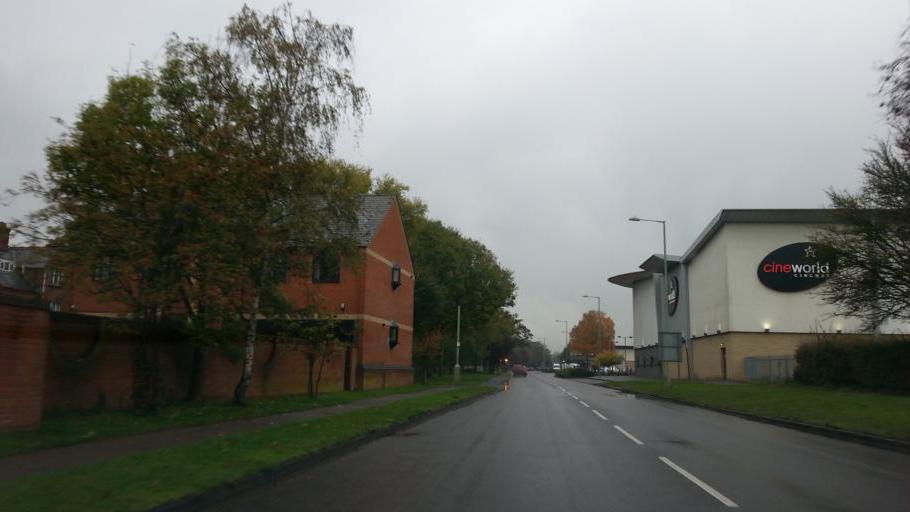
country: GB
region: England
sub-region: Suffolk
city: Haverhill
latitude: 52.0810
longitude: 0.4441
